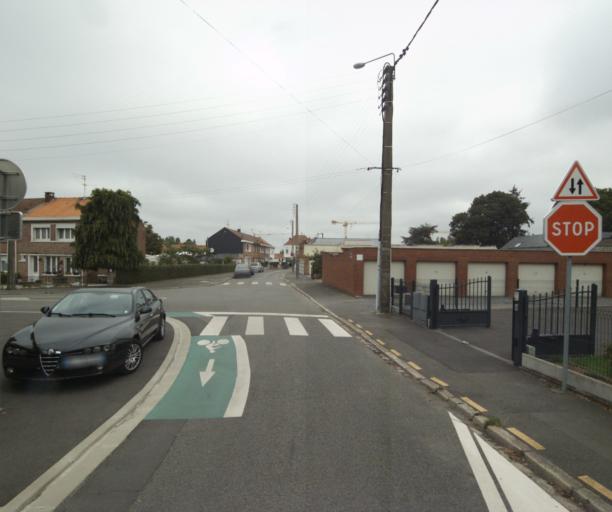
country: FR
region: Nord-Pas-de-Calais
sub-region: Departement du Nord
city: Willems
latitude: 50.6140
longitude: 3.2284
